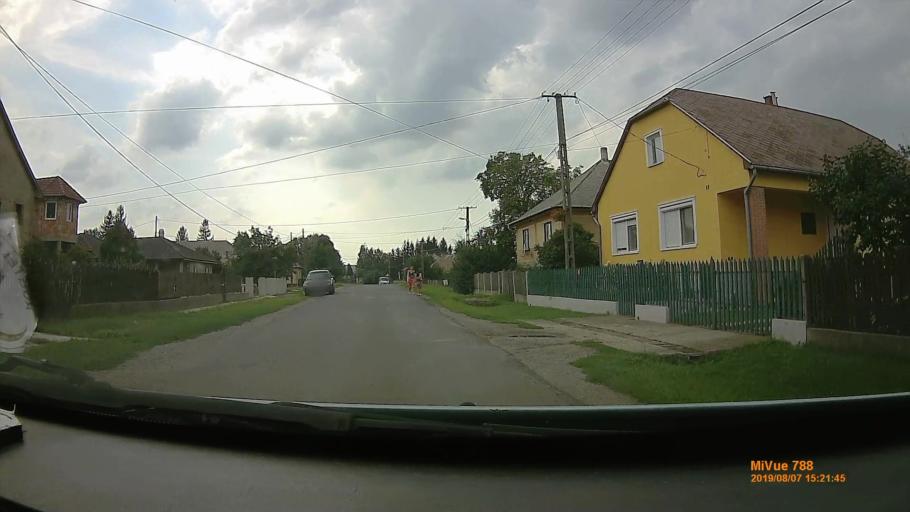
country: HU
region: Borsod-Abauj-Zemplen
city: Encs
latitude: 48.3605
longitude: 21.1502
